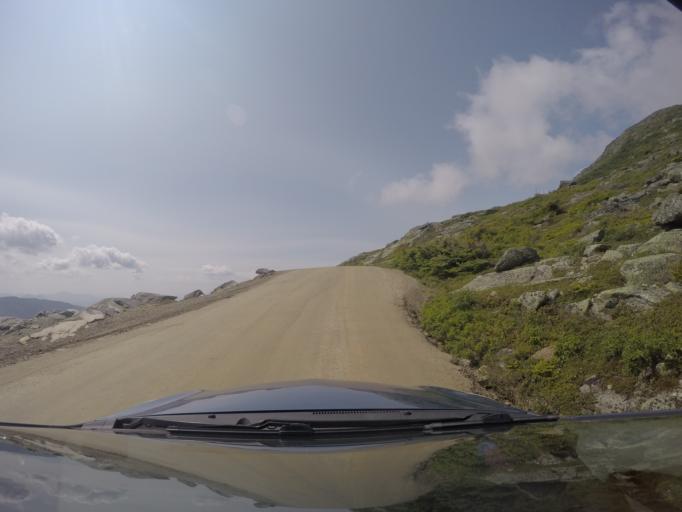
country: US
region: New Hampshire
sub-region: Coos County
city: Gorham
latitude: 44.2828
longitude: -71.2761
